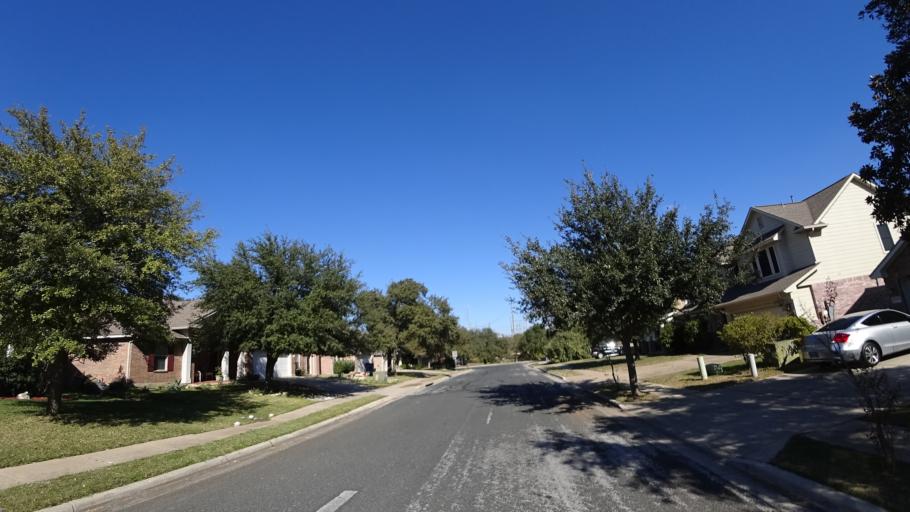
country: US
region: Texas
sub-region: Travis County
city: Wells Branch
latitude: 30.4311
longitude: -97.6902
